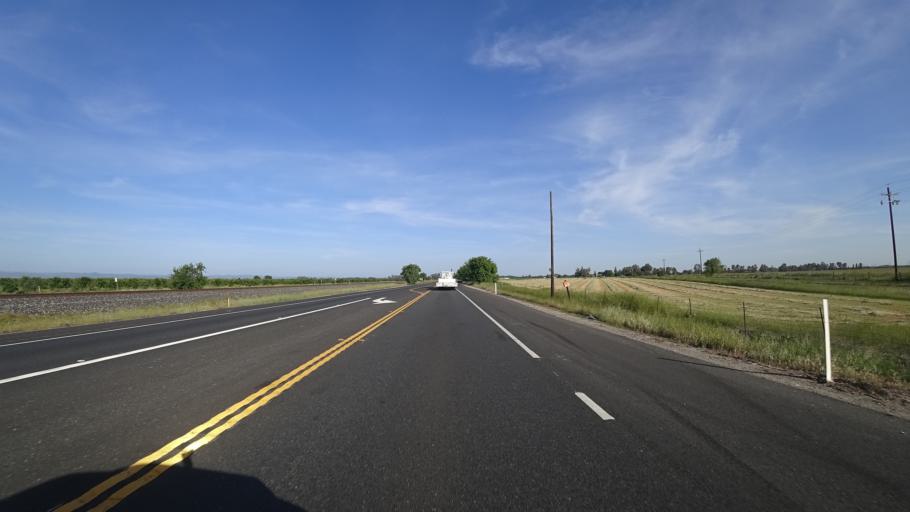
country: US
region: California
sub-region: Yuba County
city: Wheatland
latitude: 39.0344
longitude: -121.4626
